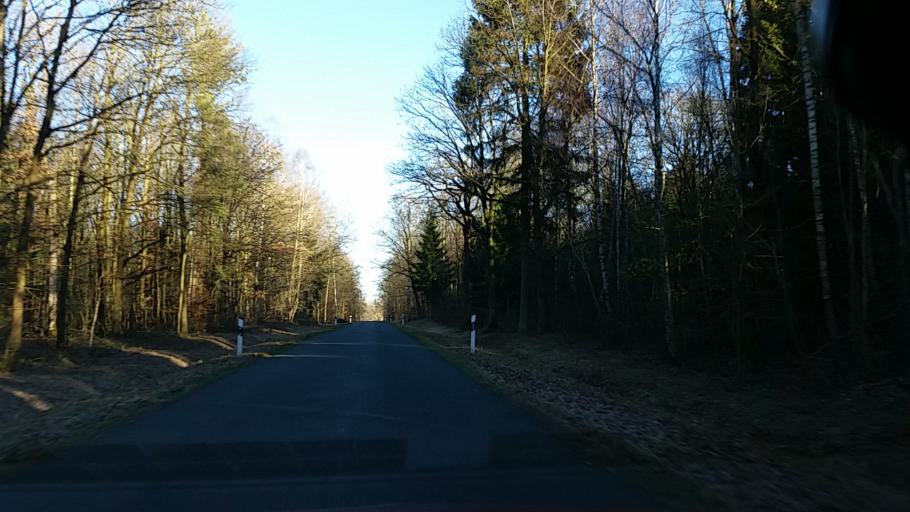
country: DE
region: Lower Saxony
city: Parsau
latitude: 52.5126
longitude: 10.9153
